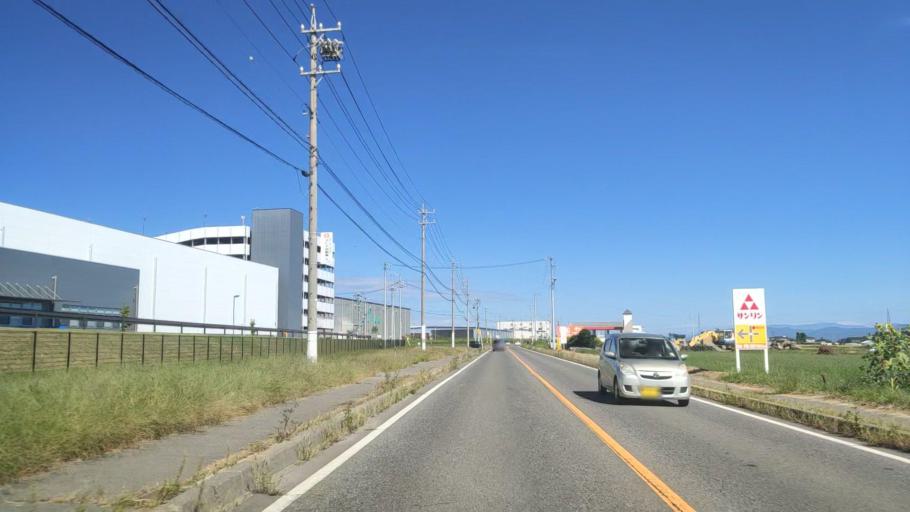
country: JP
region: Nagano
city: Matsumoto
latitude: 36.1879
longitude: 137.9033
